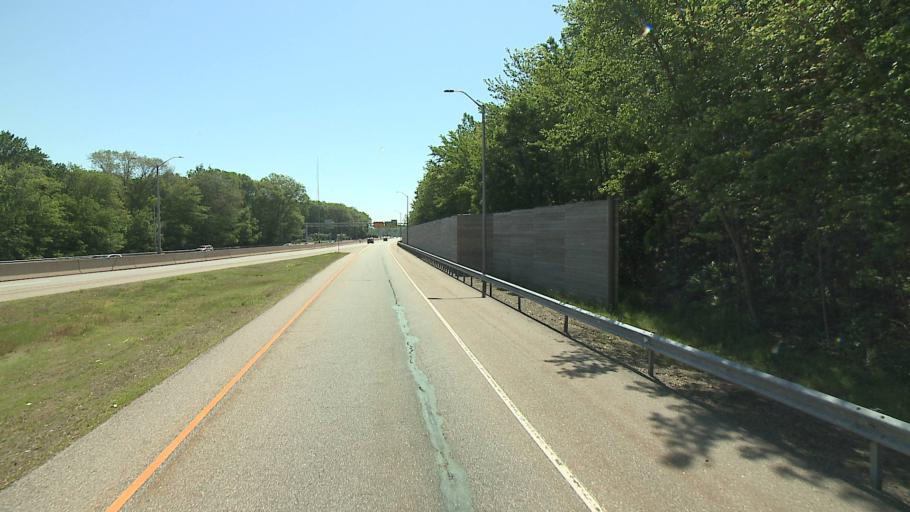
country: US
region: Connecticut
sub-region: New London County
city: Oxoboxo River
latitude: 41.4814
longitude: -72.0962
